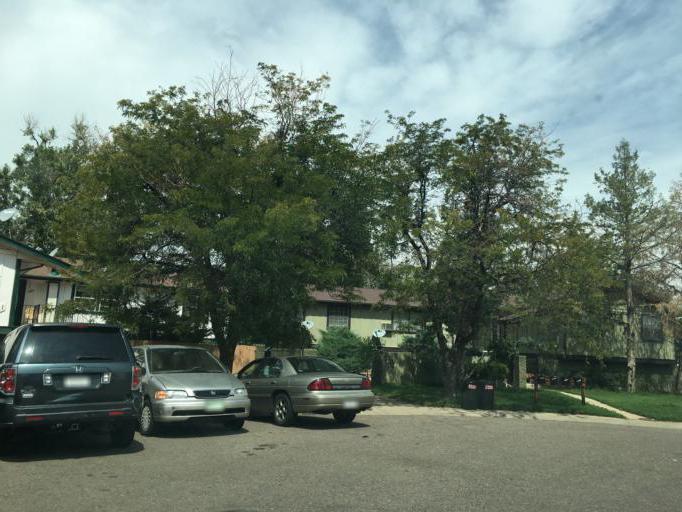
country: US
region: Colorado
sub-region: Adams County
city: Aurora
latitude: 39.7368
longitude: -104.7972
